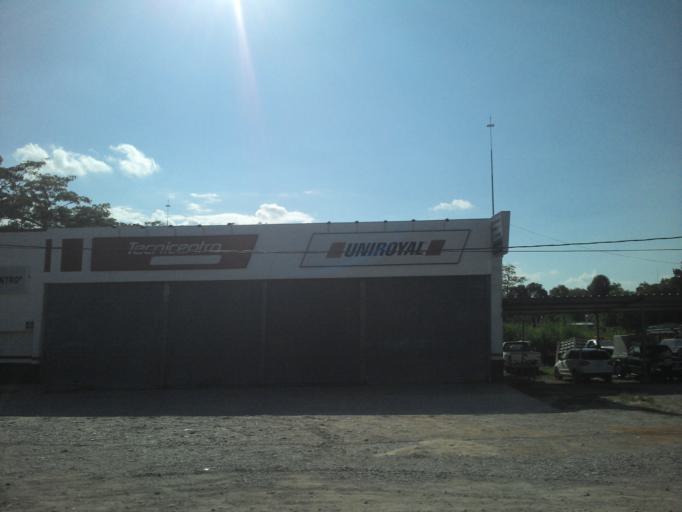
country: MX
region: Chiapas
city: Palenque
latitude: 17.5463
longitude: -91.9838
